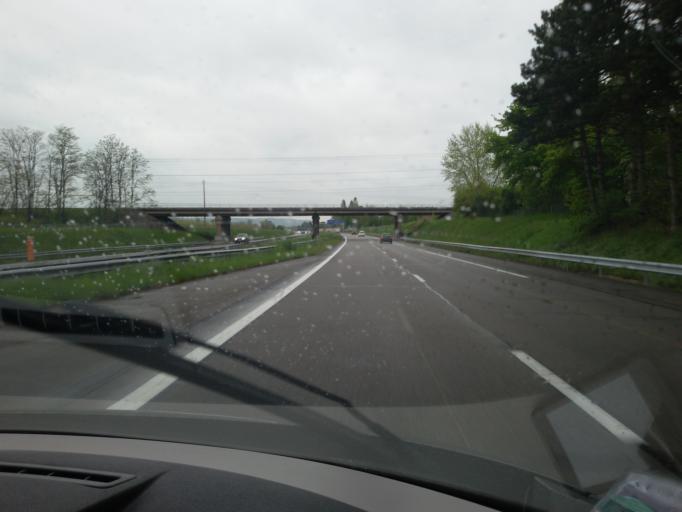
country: FR
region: Rhone-Alpes
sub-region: Departement du Rhone
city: Les Cheres
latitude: 45.8787
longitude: 4.7397
